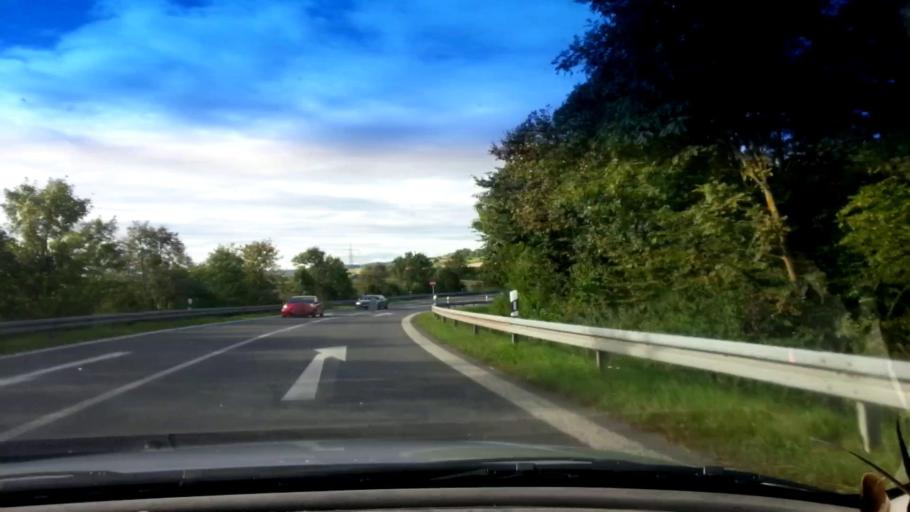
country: DE
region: Bavaria
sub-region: Upper Franconia
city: Viereth-Trunstadt
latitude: 49.9317
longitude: 10.7778
